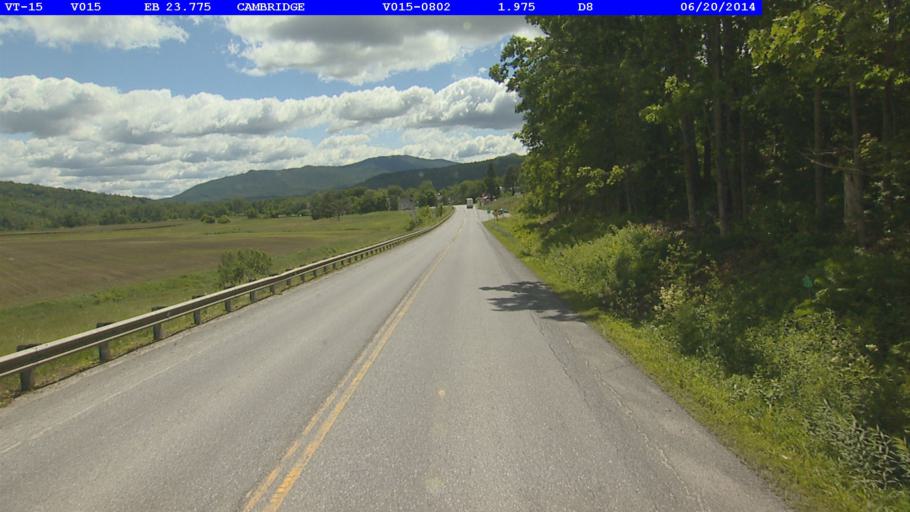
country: US
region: Vermont
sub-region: Chittenden County
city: Jericho
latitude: 44.6466
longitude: -72.8856
